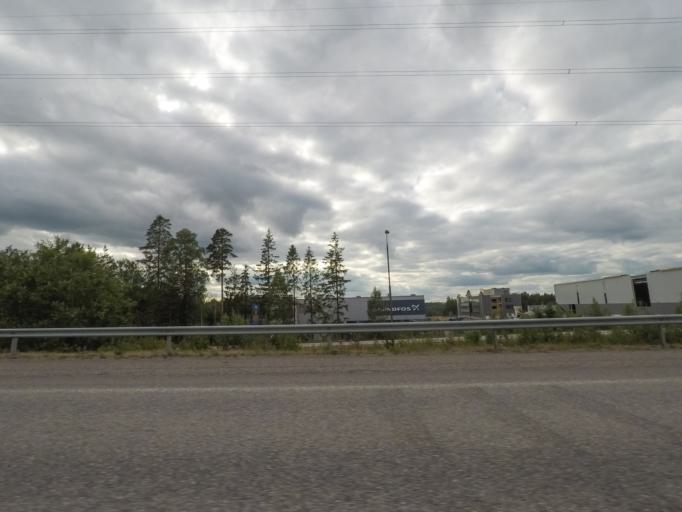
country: FI
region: Uusimaa
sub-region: Helsinki
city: Vantaa
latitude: 60.3081
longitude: 25.1004
